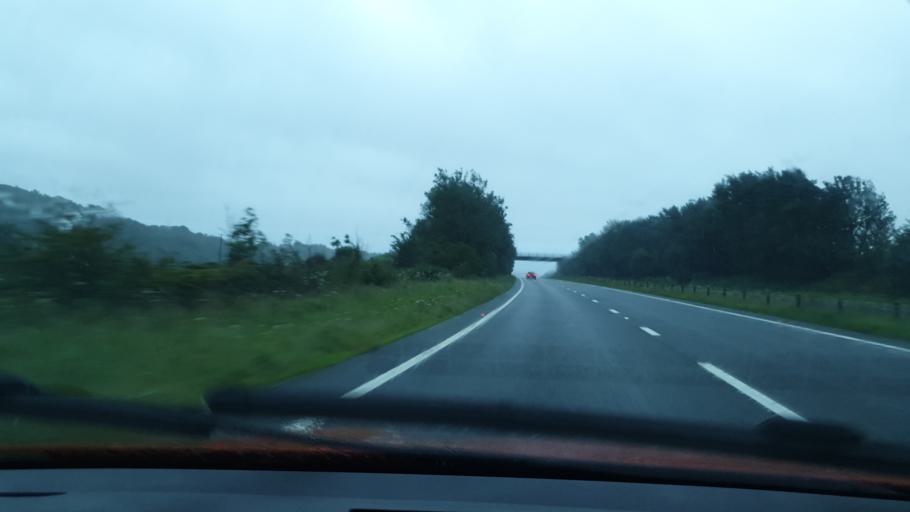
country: GB
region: England
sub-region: Cumbria
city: Grange-over-Sands
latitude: 54.2275
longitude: -2.9120
